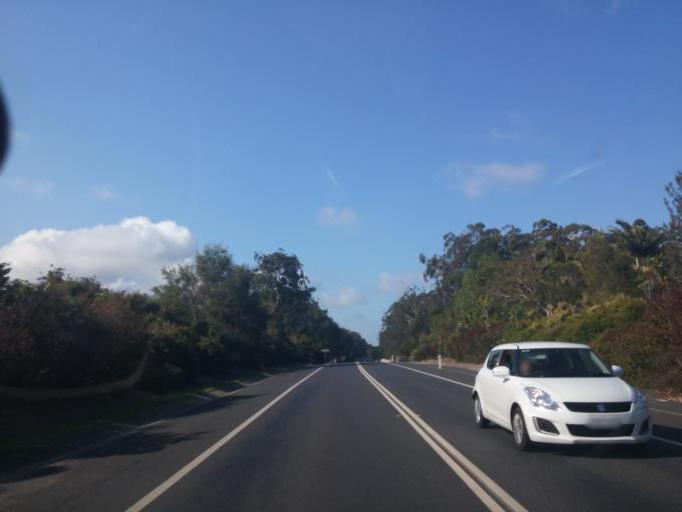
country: AU
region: New South Wales
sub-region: Coffs Harbour
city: Coffs Harbour
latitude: -30.3020
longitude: 153.1246
